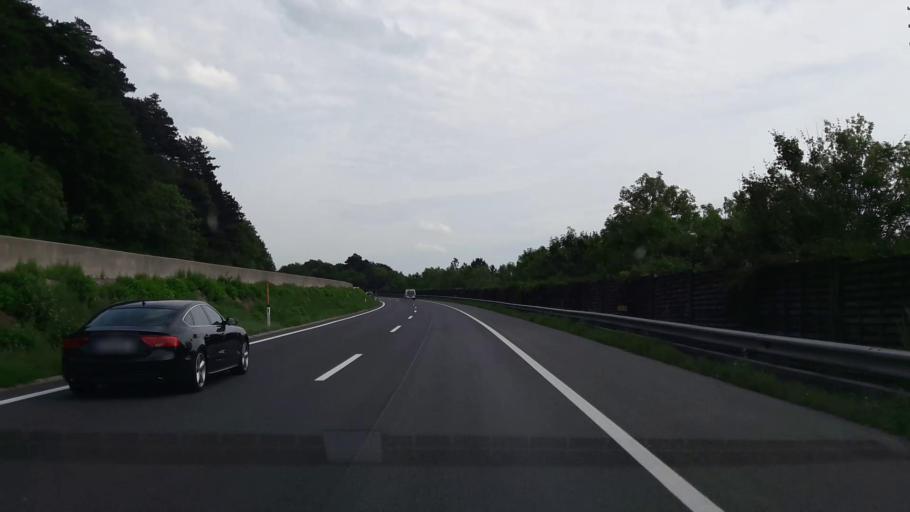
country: AT
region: Lower Austria
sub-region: Politischer Bezirk Baden
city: Alland
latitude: 48.0636
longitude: 16.0712
